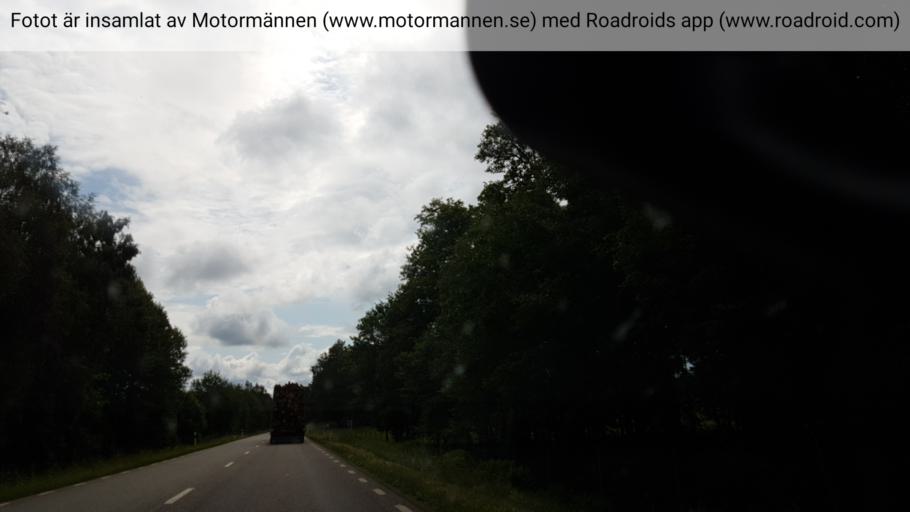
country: SE
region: Vaestra Goetaland
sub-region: Falkopings Kommun
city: Floby
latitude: 58.1919
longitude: 13.3411
